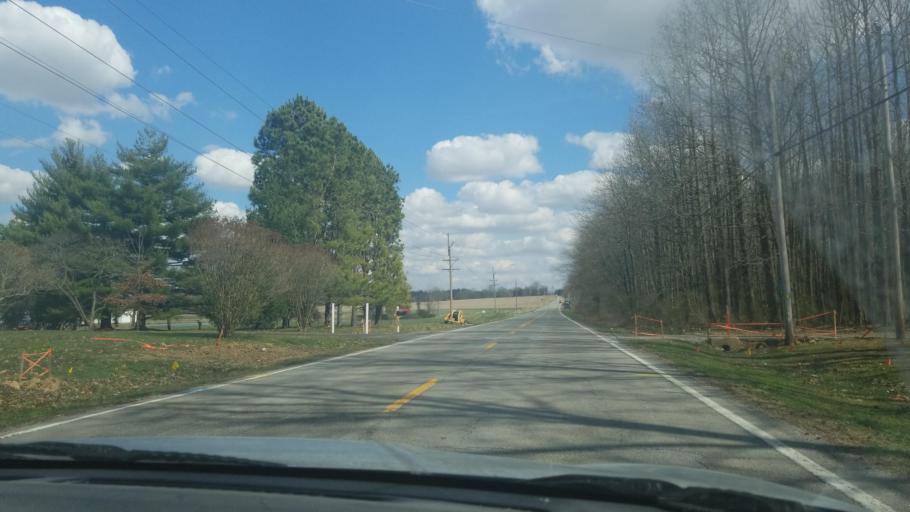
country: US
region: Illinois
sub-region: Saline County
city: Harrisburg
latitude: 37.7388
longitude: -88.5887
